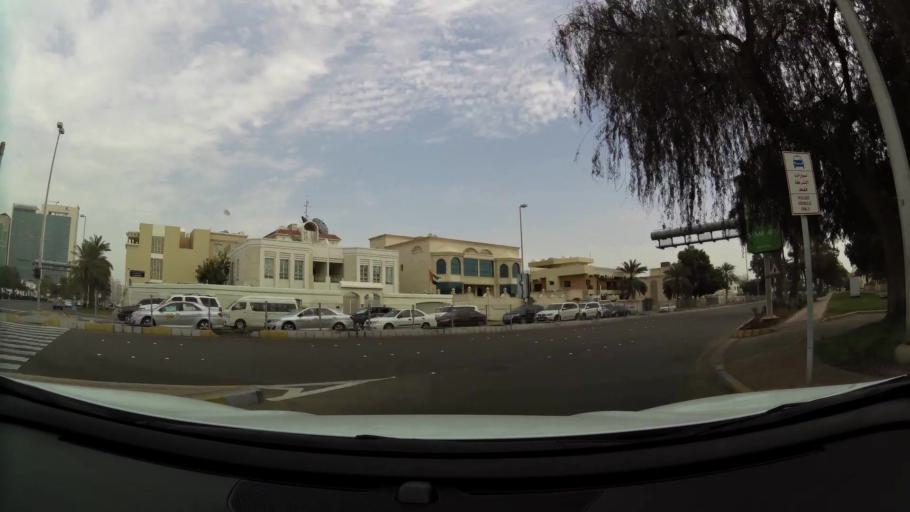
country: AE
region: Abu Dhabi
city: Abu Dhabi
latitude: 24.4658
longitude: 54.3660
